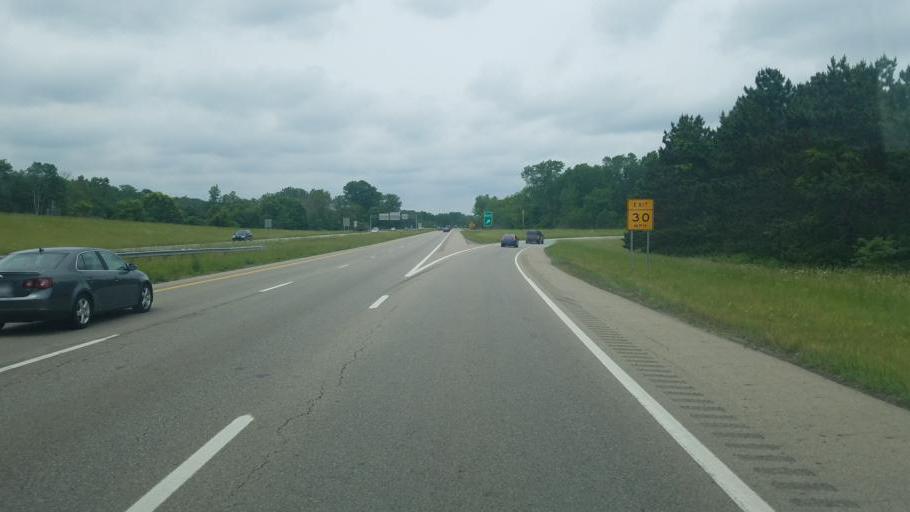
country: US
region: Ohio
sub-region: Licking County
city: Granville
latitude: 40.0612
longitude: -82.5291
